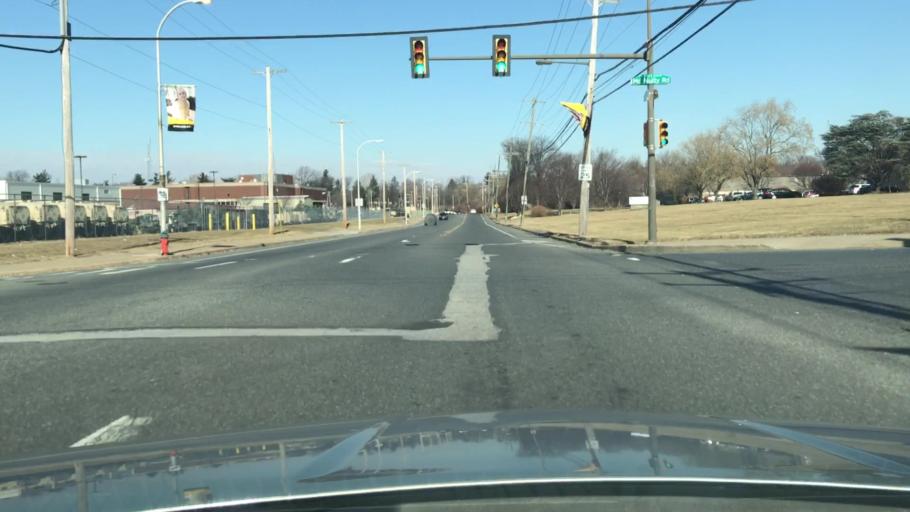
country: US
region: Pennsylvania
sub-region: Bucks County
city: Trevose
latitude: 40.1096
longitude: -74.9868
